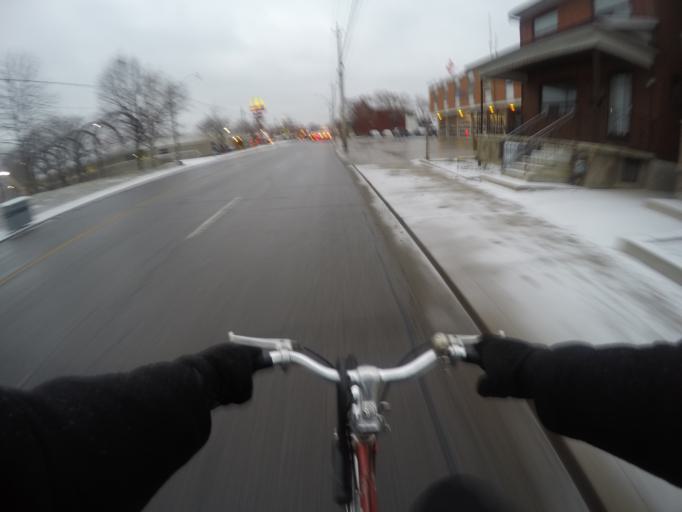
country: CA
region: Ontario
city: Toronto
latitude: 43.6663
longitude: -79.4373
